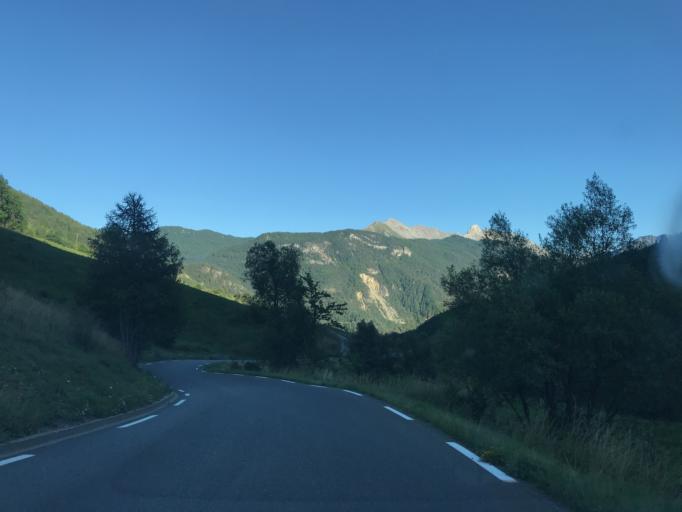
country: FR
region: Provence-Alpes-Cote d'Azur
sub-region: Departement des Hautes-Alpes
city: Guillestre
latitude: 44.7581
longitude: 6.7483
